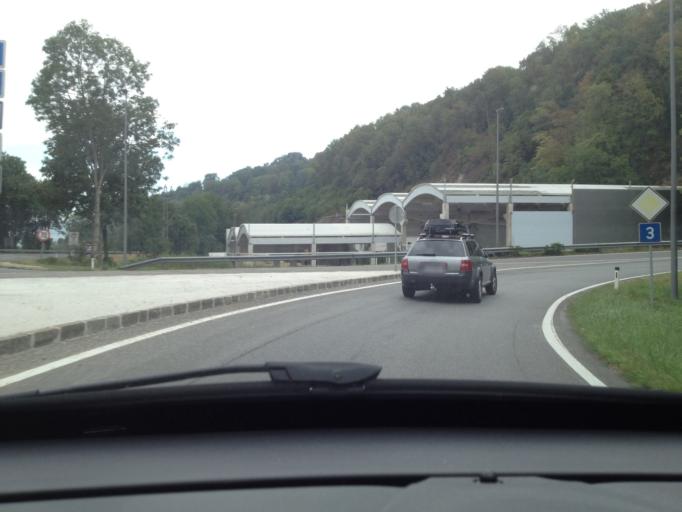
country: AT
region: Upper Austria
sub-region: Politischer Bezirk Urfahr-Umgebung
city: Steyregg
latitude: 48.2897
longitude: 14.3460
